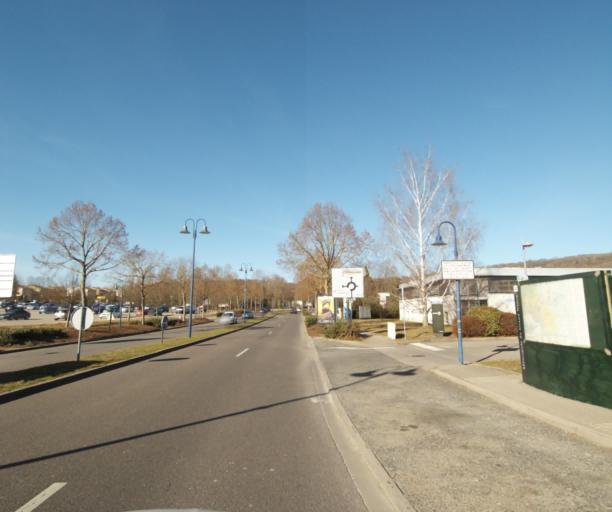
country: FR
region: Lorraine
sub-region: Departement de Meurthe-et-Moselle
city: Ludres
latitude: 48.6188
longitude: 6.1761
